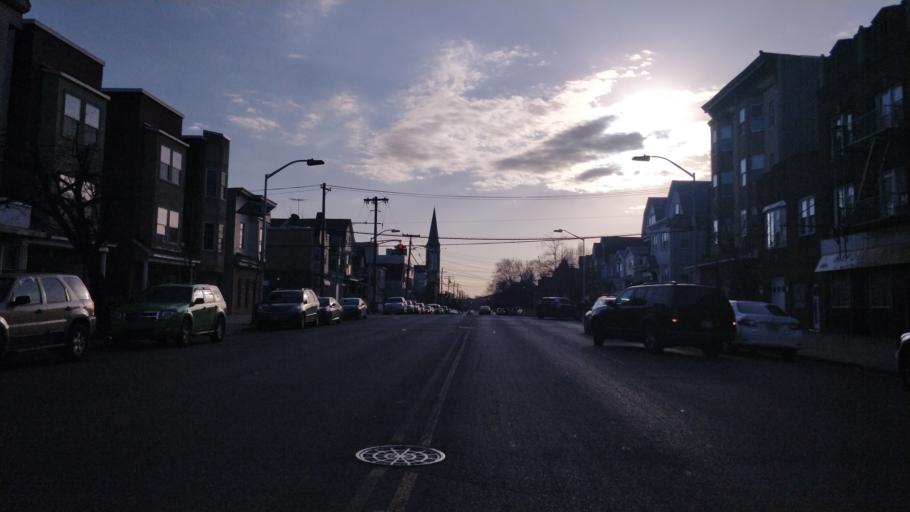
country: US
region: New Jersey
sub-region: Hudson County
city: Bayonne
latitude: 40.6606
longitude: -74.1244
